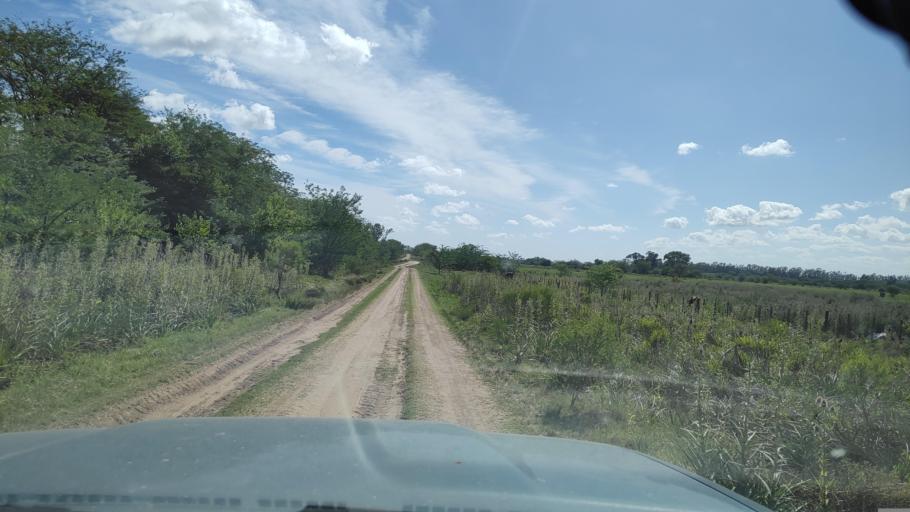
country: AR
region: Buenos Aires
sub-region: Partido de Lujan
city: Lujan
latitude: -34.5222
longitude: -59.1707
